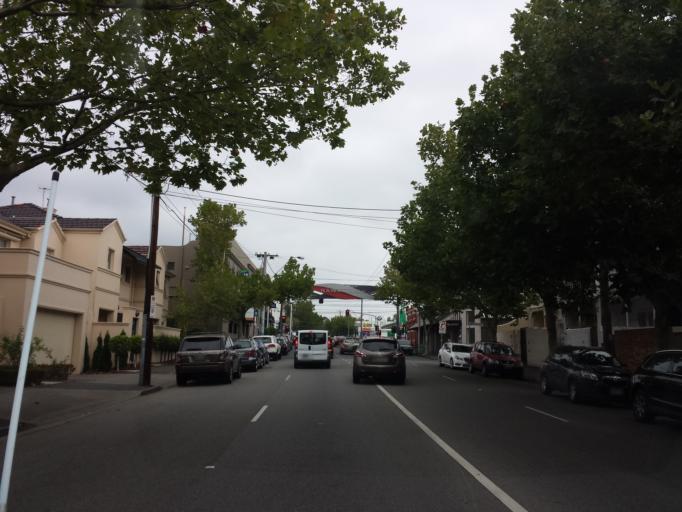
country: AU
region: Victoria
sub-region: Stonnington
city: Toorak
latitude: -37.8472
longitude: 145.0034
